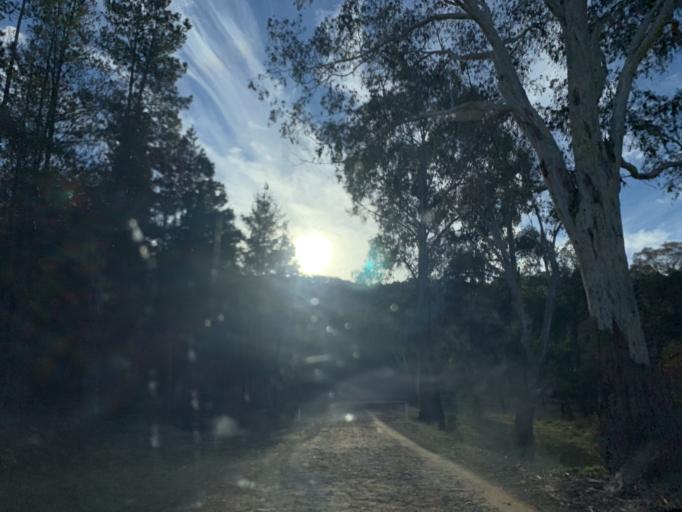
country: AU
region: Victoria
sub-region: Mansfield
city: Mansfield
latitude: -36.9339
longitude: 146.0931
